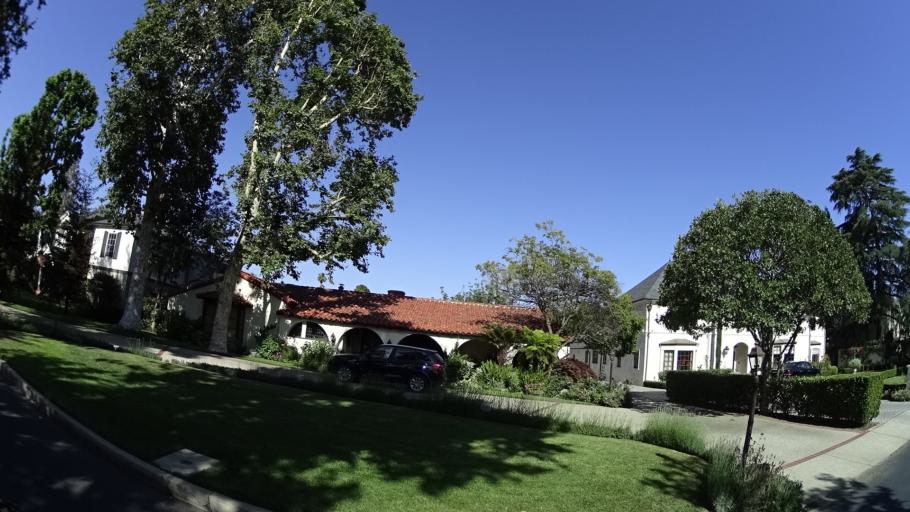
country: US
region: California
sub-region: Los Angeles County
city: Universal City
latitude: 34.1462
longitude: -118.3600
